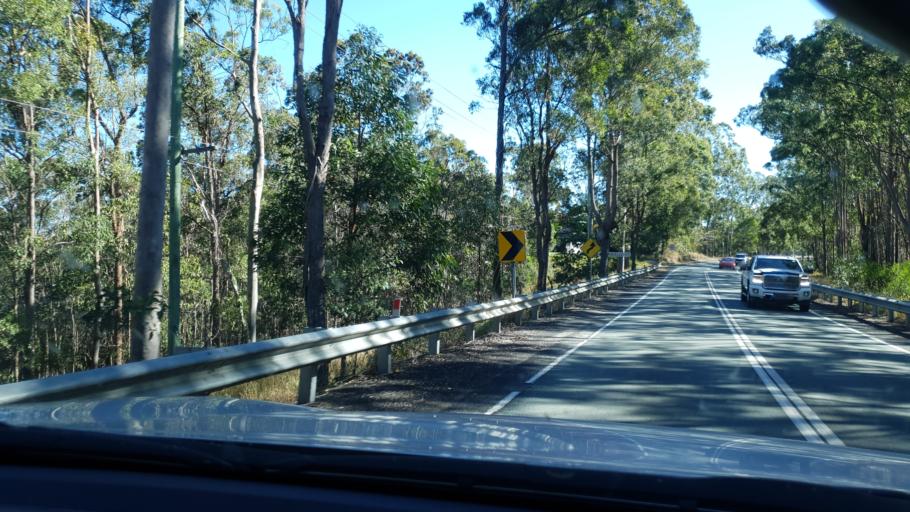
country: AU
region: Queensland
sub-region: Moreton Bay
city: Ferny Hills
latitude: -27.3312
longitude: 152.9285
